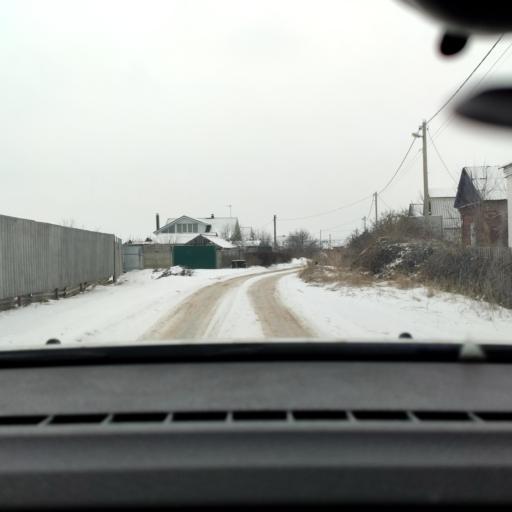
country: RU
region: Voronezj
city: Podgornoye
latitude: 51.7941
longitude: 39.1437
